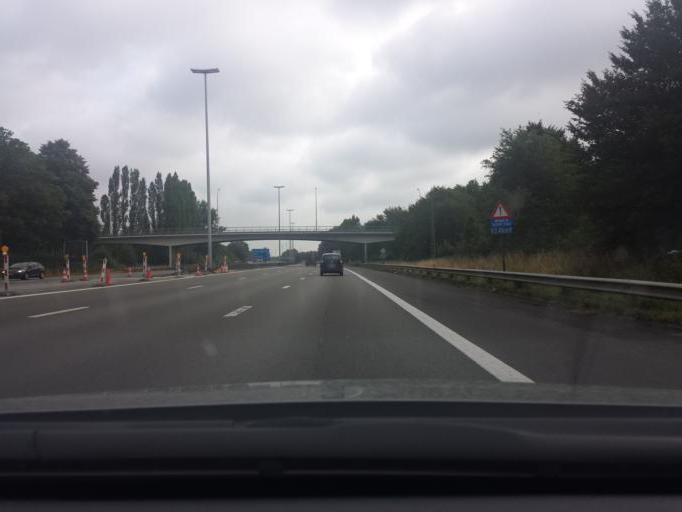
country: BE
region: Flanders
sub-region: Provincie West-Vlaanderen
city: Waregem
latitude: 50.8773
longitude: 3.4547
